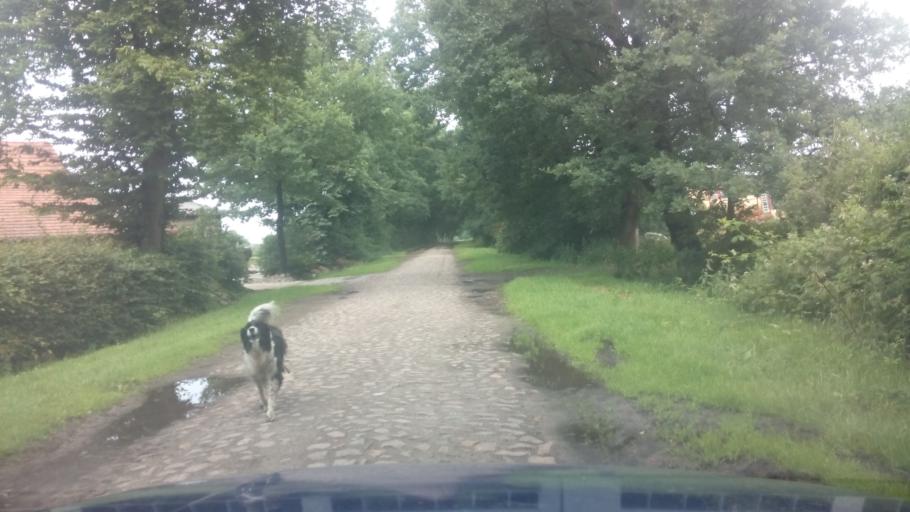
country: DE
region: Lower Saxony
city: Osterholz-Scharmbeck
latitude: 53.2355
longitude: 8.7488
